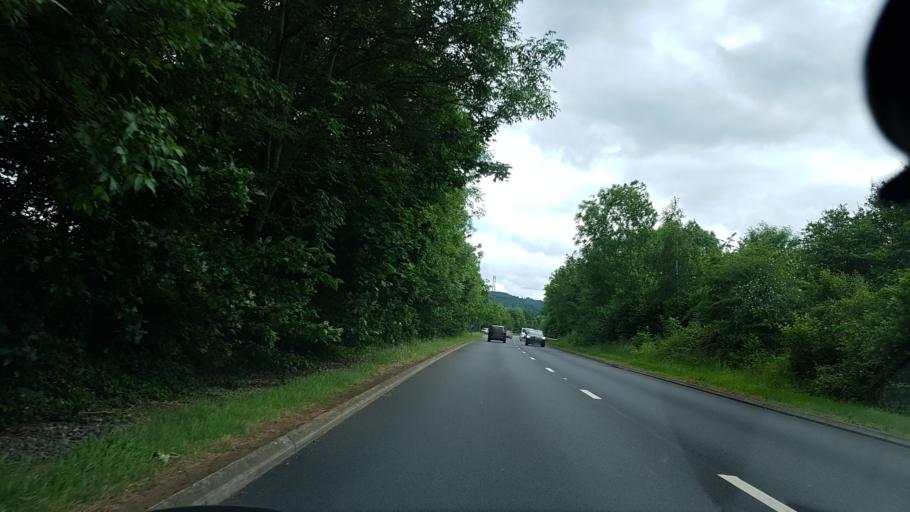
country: GB
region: Wales
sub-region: Monmouthshire
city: Abergavenny
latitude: 51.8445
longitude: -2.9999
